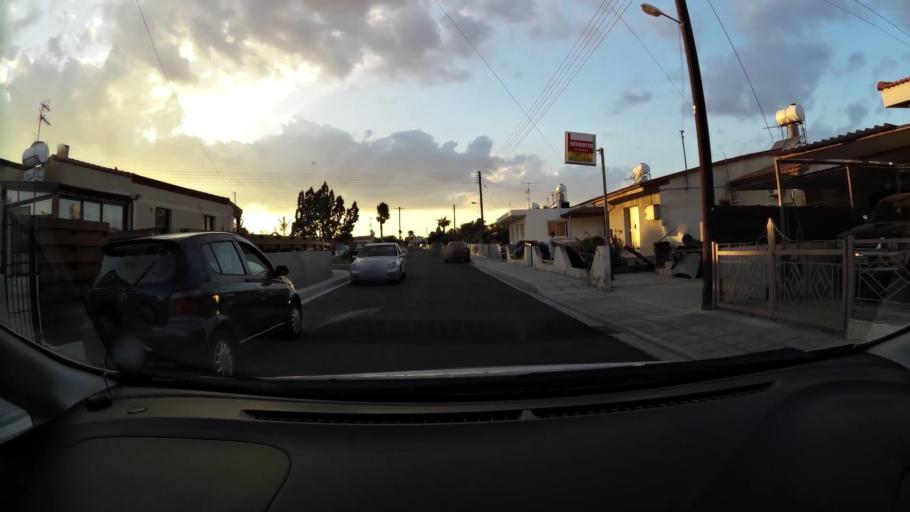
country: CY
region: Larnaka
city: Dhromolaxia
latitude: 34.8696
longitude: 33.5872
